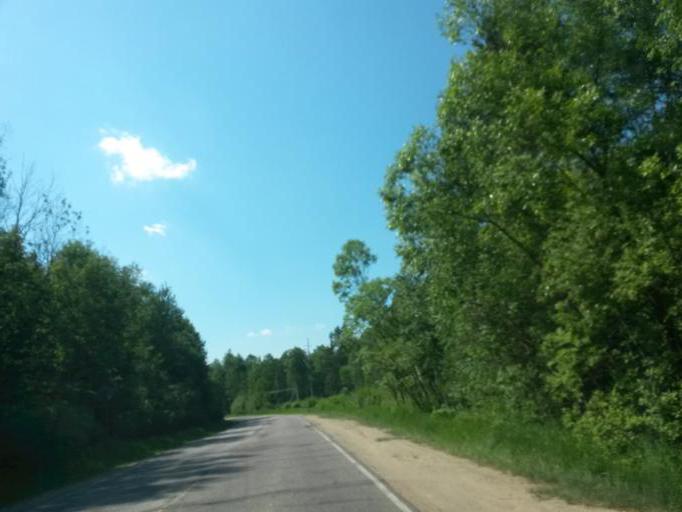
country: RU
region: Moskovskaya
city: Danki
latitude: 54.9094
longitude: 37.5511
